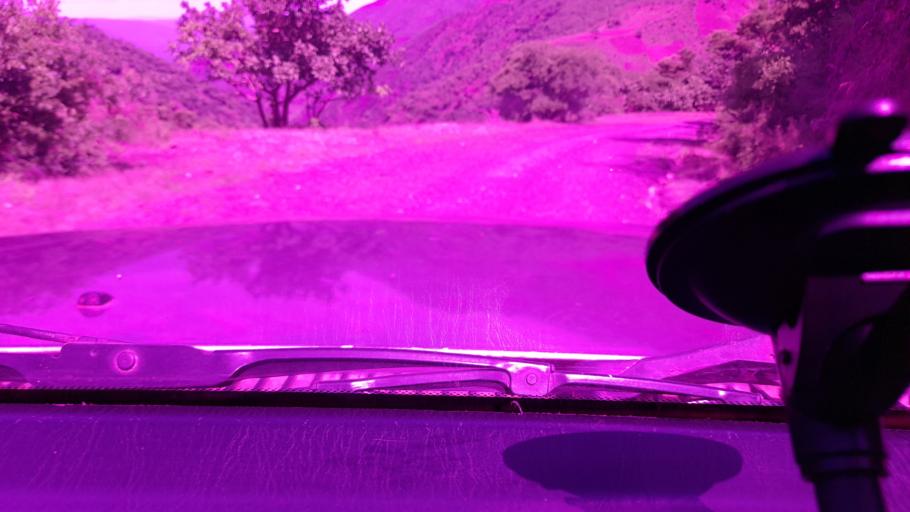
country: ET
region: Oromiya
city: Jima
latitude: 7.8045
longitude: 37.5271
